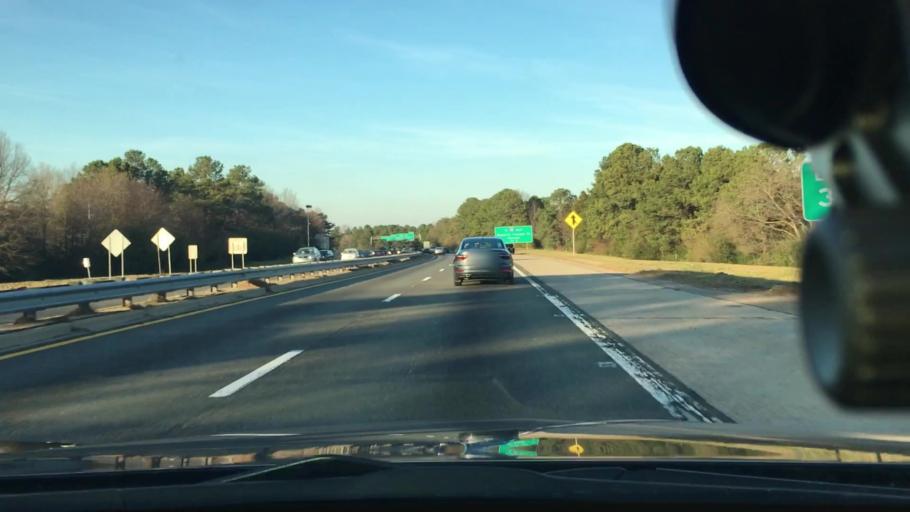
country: US
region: North Carolina
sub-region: Wake County
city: West Raleigh
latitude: 35.7966
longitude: -78.6944
